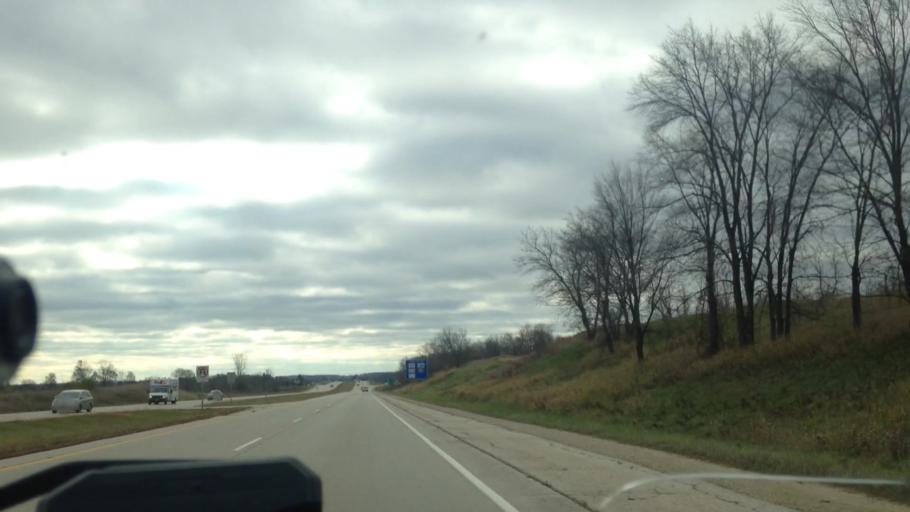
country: US
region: Wisconsin
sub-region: Washington County
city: Jackson
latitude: 43.3343
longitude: -88.1901
